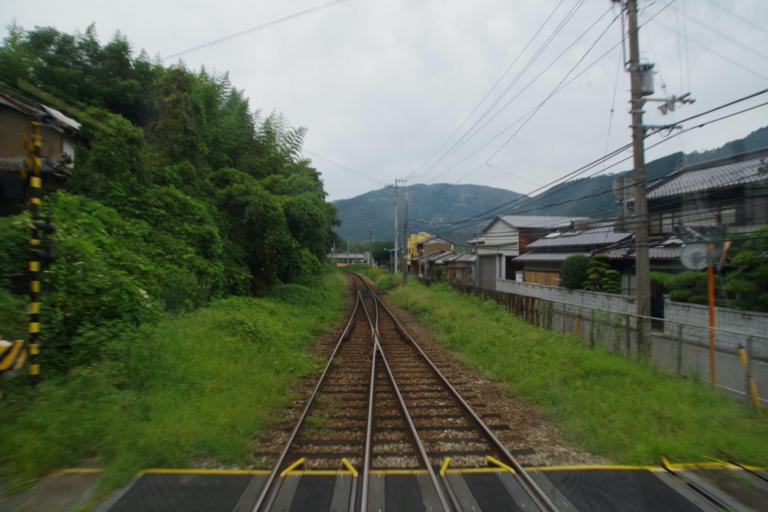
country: JP
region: Tokushima
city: Ikedacho
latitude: 34.0326
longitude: 133.8556
